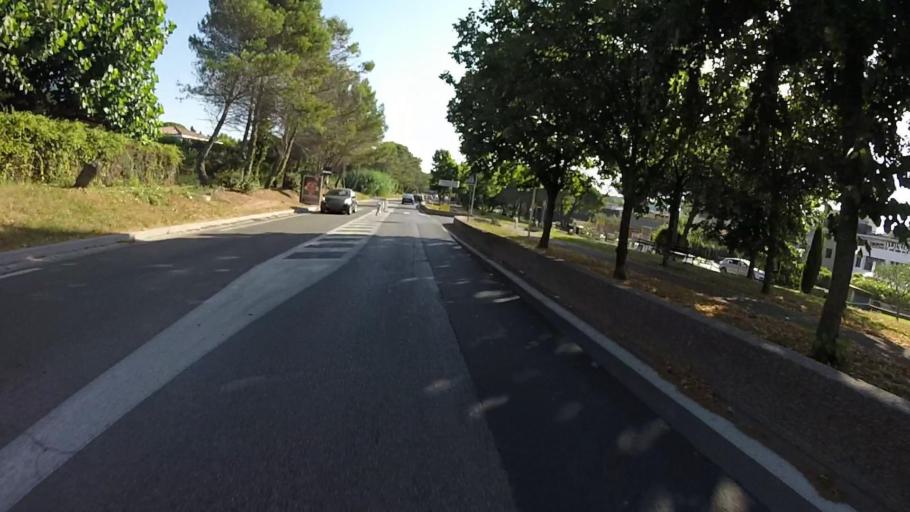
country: FR
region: Provence-Alpes-Cote d'Azur
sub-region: Departement des Alpes-Maritimes
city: Mougins
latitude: 43.6095
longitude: 7.0107
